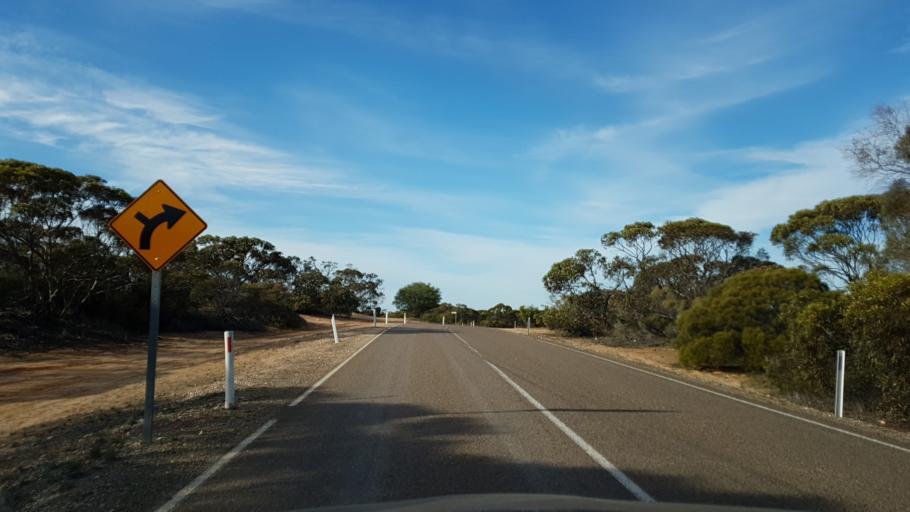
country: AU
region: South Australia
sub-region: Mid Murray
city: Mannum
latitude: -35.0433
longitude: 139.4650
